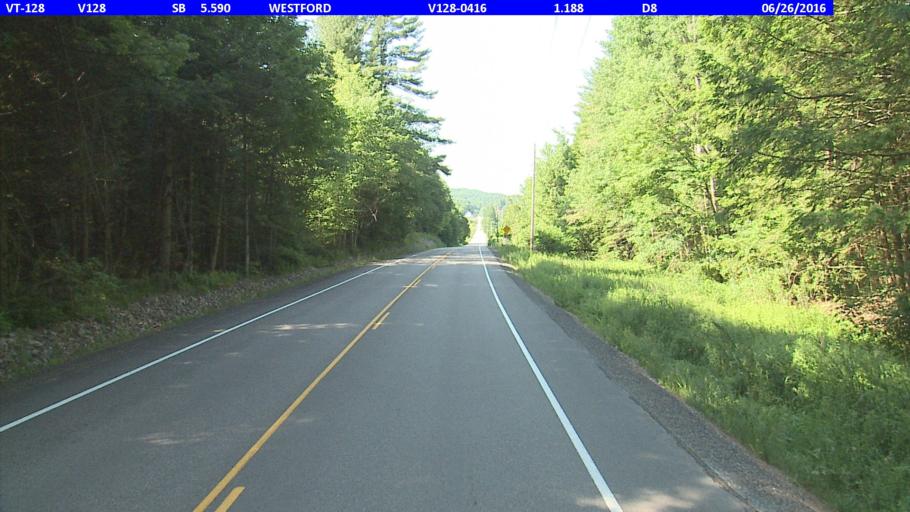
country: US
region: Vermont
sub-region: Chittenden County
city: Jericho
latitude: 44.5752
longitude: -73.0202
